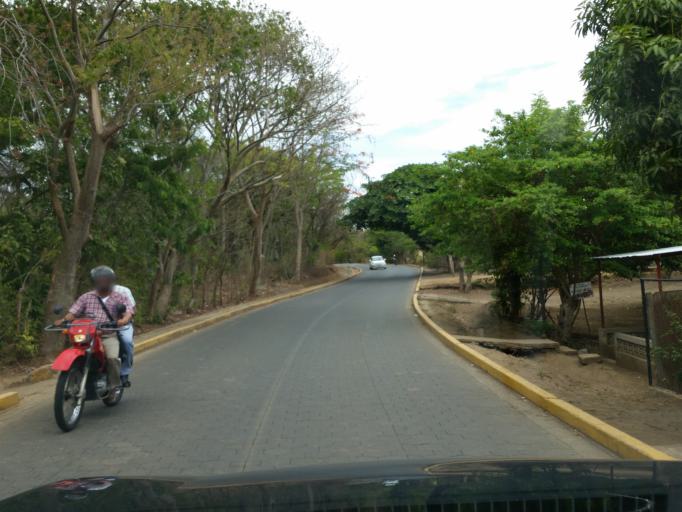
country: NI
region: Masaya
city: Masaya
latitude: 11.9920
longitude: -86.0396
